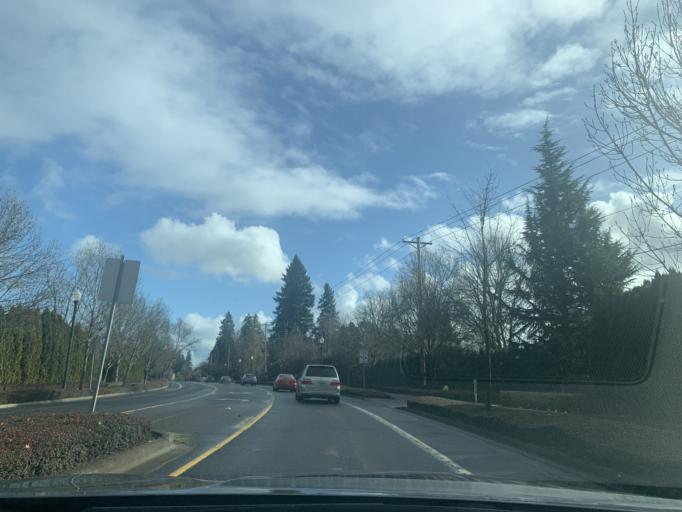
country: US
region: Oregon
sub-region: Washington County
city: Sherwood
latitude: 45.3715
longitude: -122.8548
